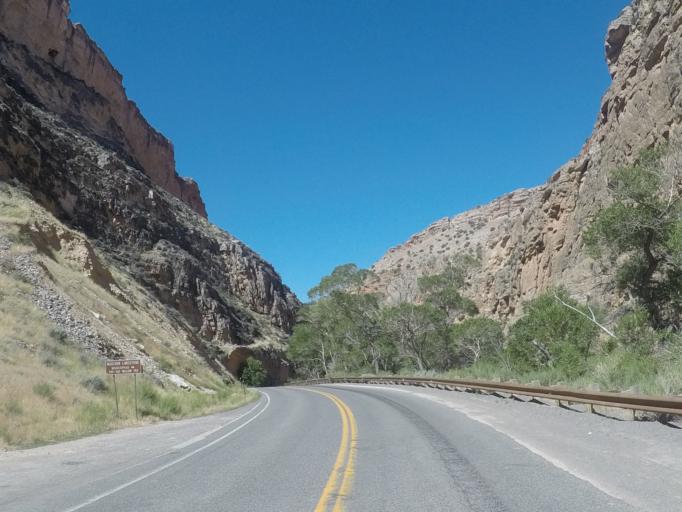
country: US
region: Wyoming
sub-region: Big Horn County
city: Greybull
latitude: 44.5748
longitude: -107.6983
